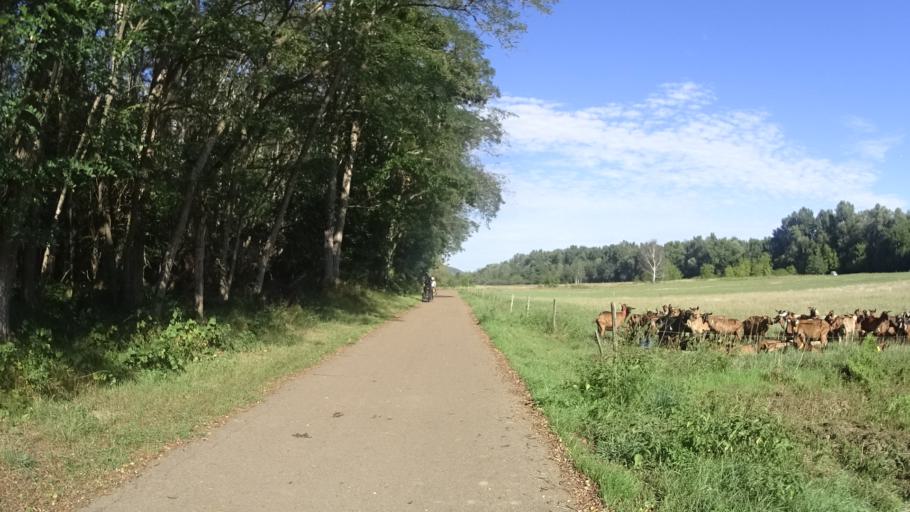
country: FR
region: Centre
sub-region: Departement du Cher
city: Sancerre
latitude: 47.3129
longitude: 2.8822
